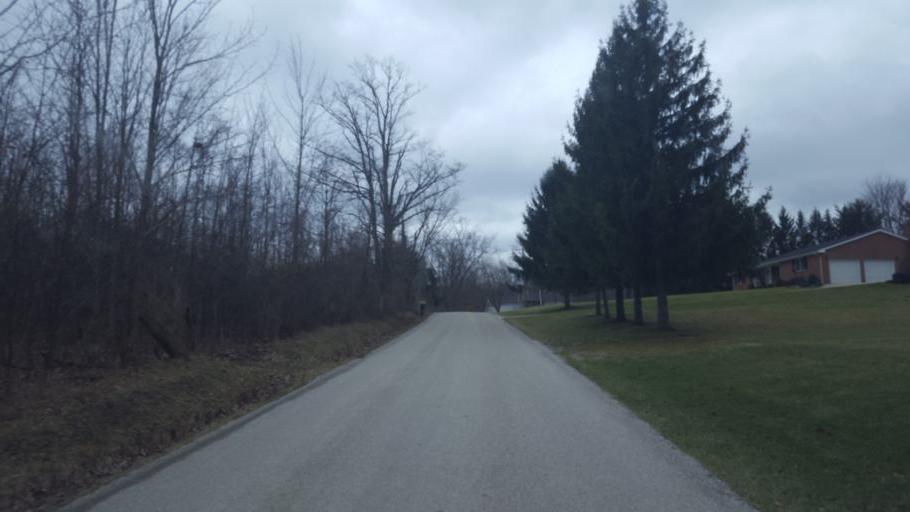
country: US
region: Ohio
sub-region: Richland County
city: Ontario
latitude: 40.7847
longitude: -82.6456
